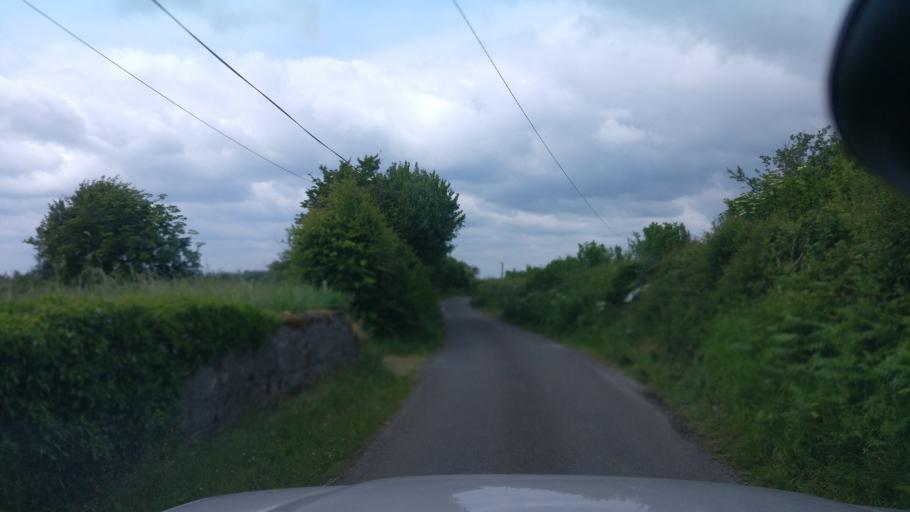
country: IE
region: Connaught
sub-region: County Galway
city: Ballinasloe
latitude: 53.2935
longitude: -8.3179
